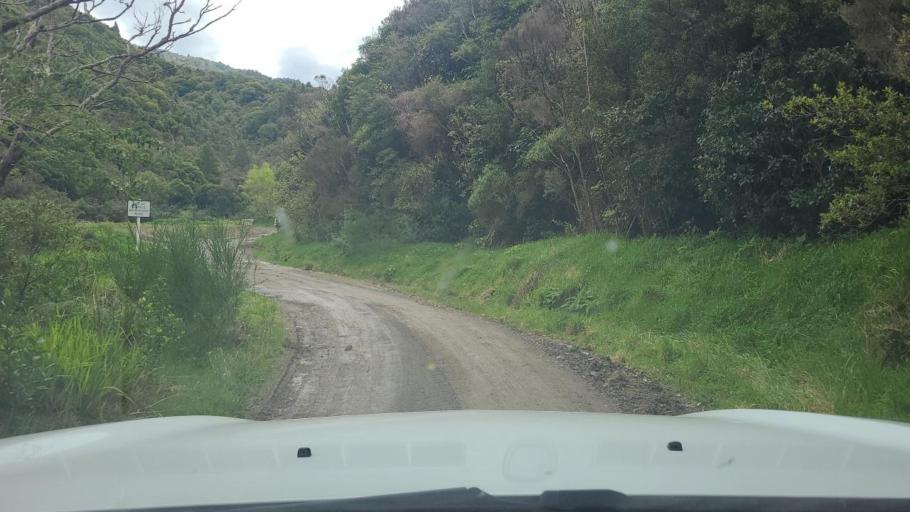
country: NZ
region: Wellington
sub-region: Masterton District
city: Masterton
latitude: -40.9495
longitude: 175.4506
